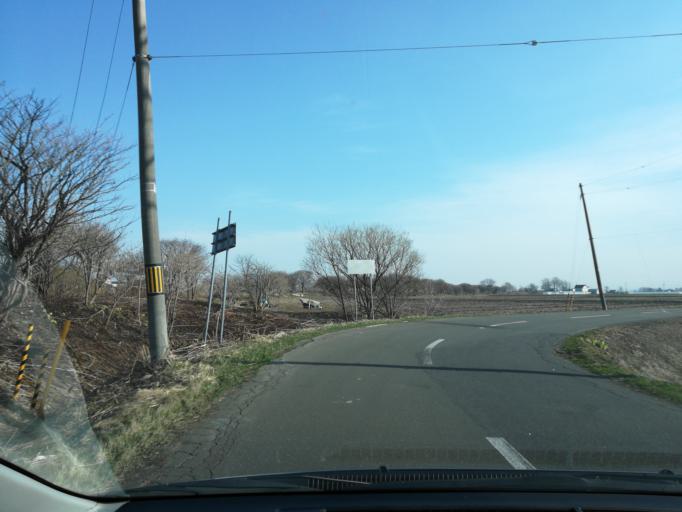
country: JP
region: Hokkaido
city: Ebetsu
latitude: 43.1565
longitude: 141.6413
